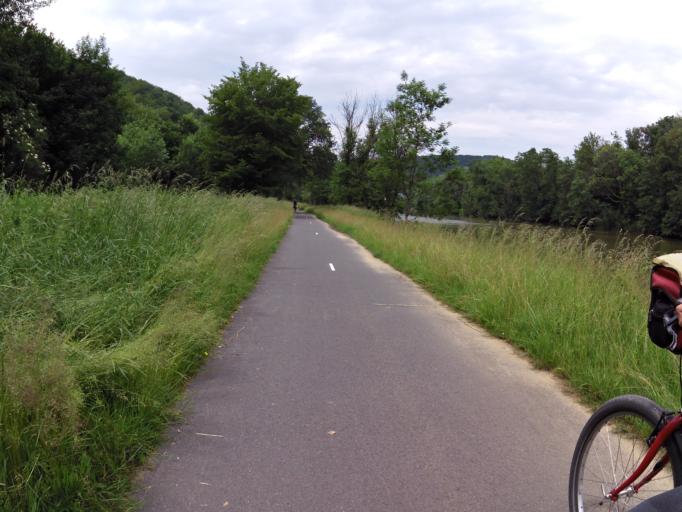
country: FR
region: Champagne-Ardenne
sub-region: Departement des Ardennes
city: Nouzonville
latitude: 49.8061
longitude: 4.7454
